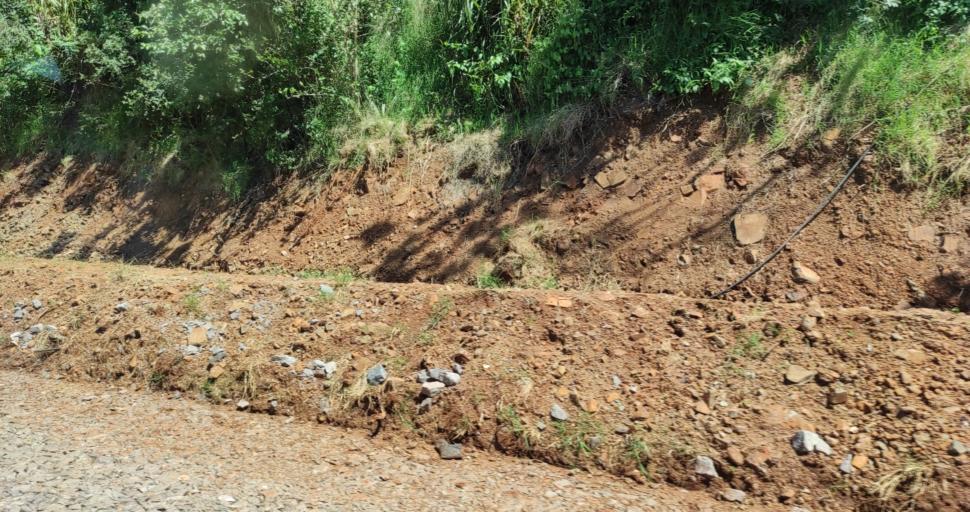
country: AR
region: Misiones
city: El Soberbio
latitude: -27.2879
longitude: -54.2155
